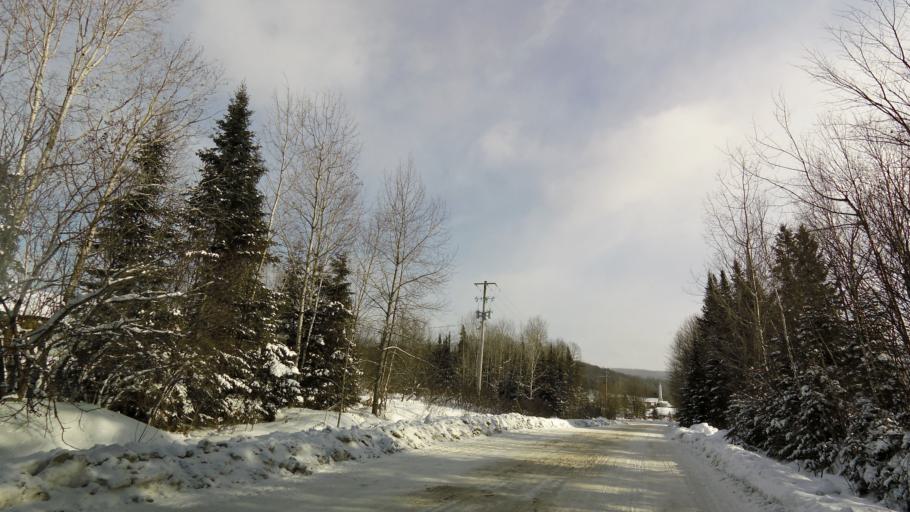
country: CA
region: Ontario
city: Bancroft
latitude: 45.0533
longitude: -78.5407
